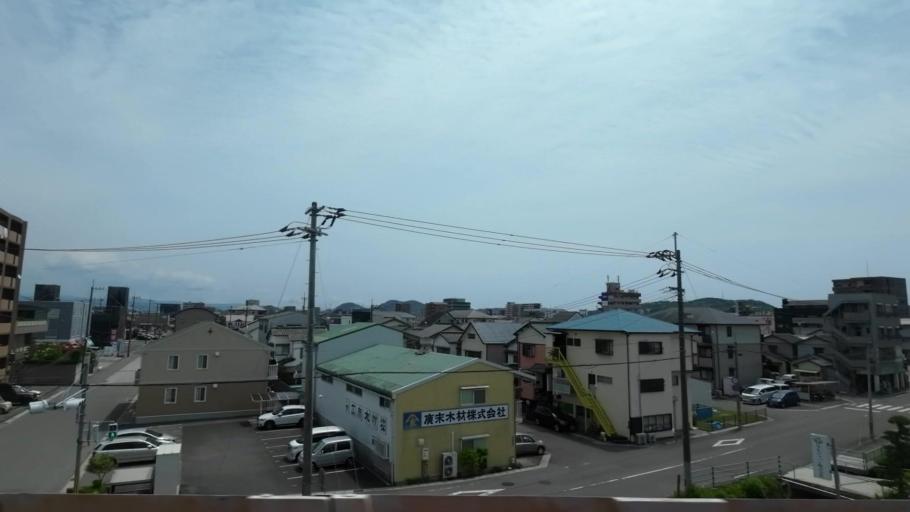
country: JP
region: Kochi
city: Kochi-shi
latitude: 33.5710
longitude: 133.5534
